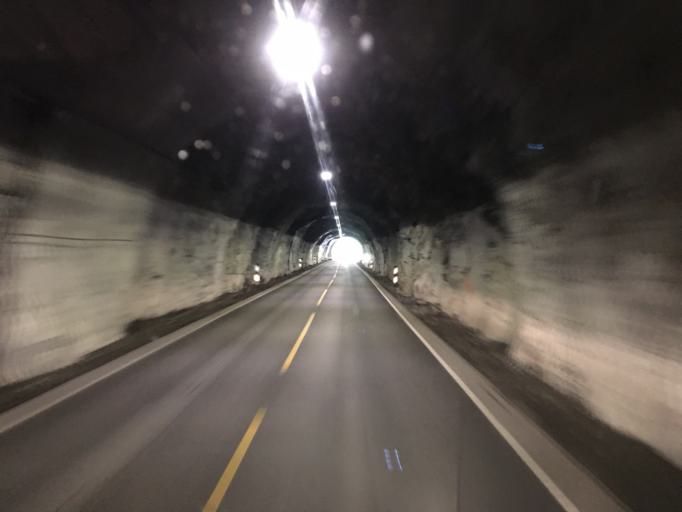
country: NO
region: More og Romsdal
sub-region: Tingvoll
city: Tingvoll
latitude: 62.9713
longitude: 8.0749
